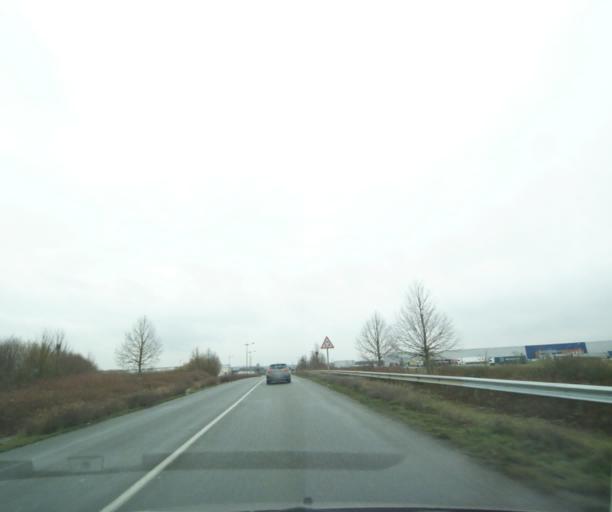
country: FR
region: Nord-Pas-de-Calais
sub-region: Departement du Nord
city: Prouvy
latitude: 50.3370
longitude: 3.4444
